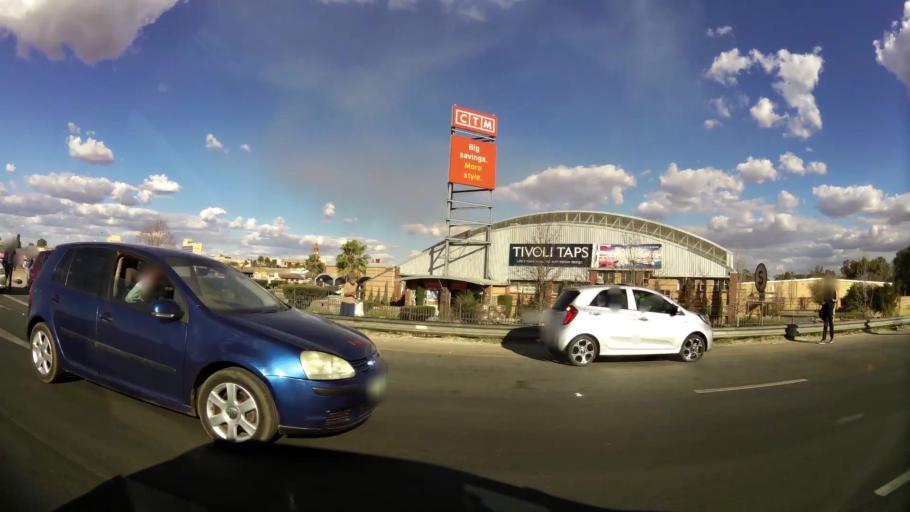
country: ZA
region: North-West
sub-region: Dr Kenneth Kaunda District Municipality
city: Klerksdorp
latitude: -26.8633
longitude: 26.6594
